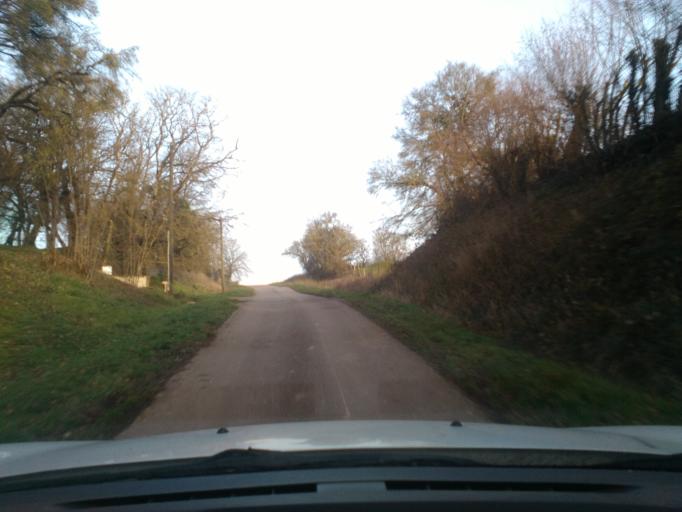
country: FR
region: Lorraine
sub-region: Departement des Vosges
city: Vittel
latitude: 48.2536
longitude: 6.0013
